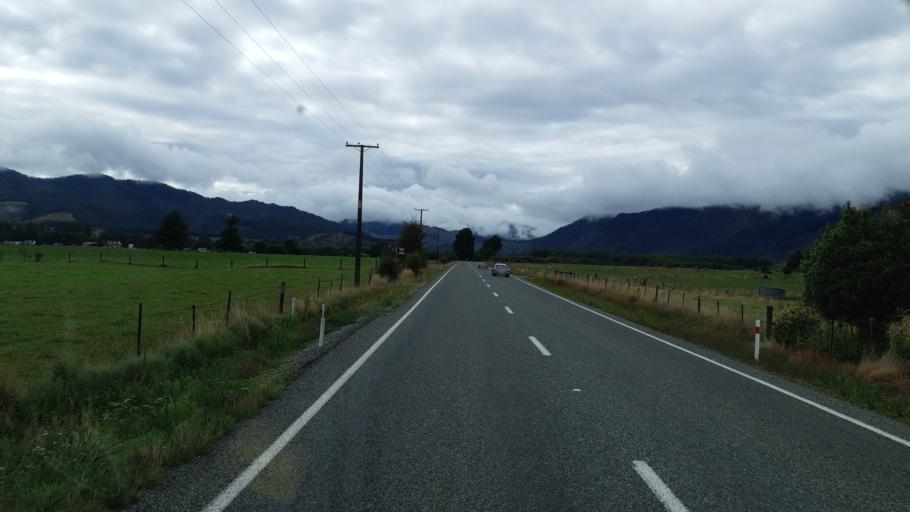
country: NZ
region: West Coast
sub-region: Buller District
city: Westport
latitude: -41.7949
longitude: 172.3014
